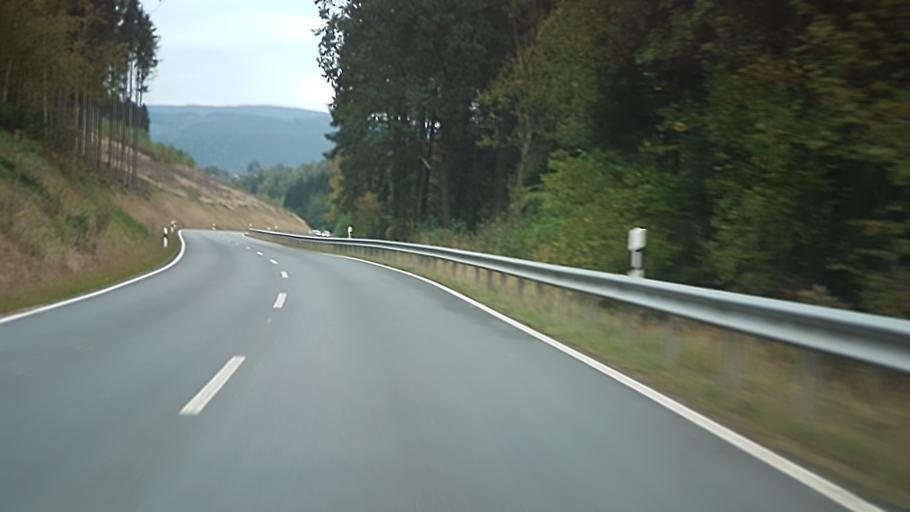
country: DE
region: North Rhine-Westphalia
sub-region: Regierungsbezirk Arnsberg
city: Attendorn
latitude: 51.1404
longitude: 7.8793
